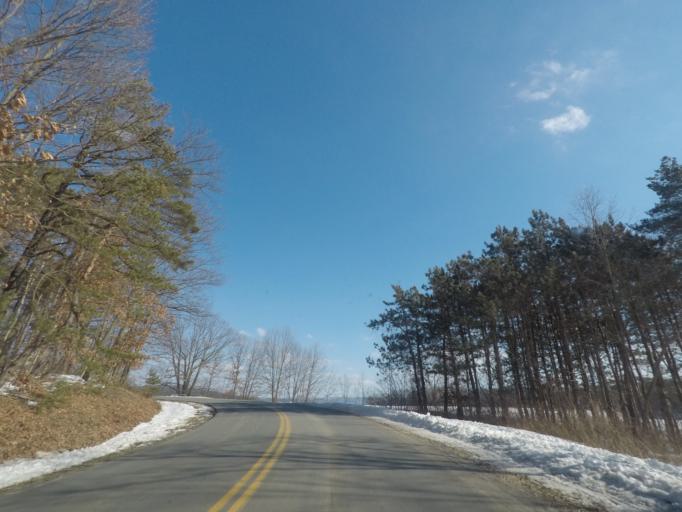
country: US
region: New York
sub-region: Saratoga County
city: Stillwater
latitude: 42.8686
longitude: -73.5854
